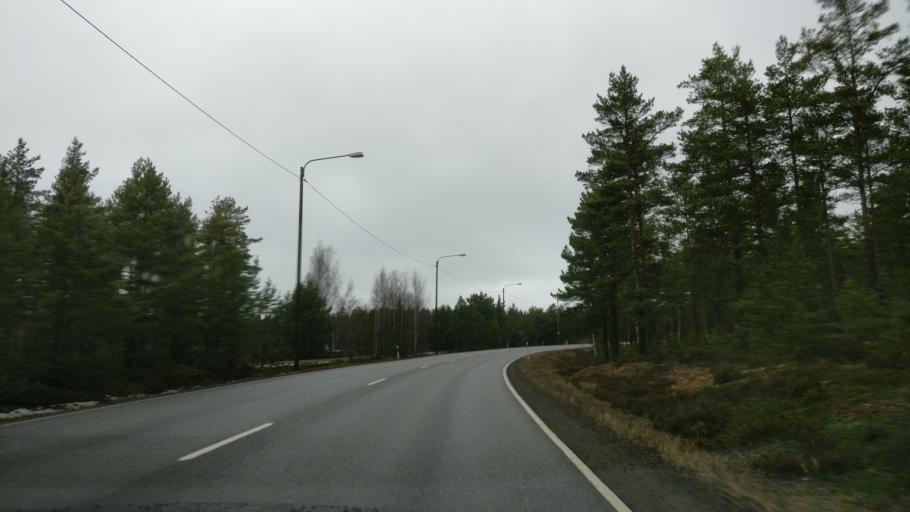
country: FI
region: Uusimaa
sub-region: Raaseporin
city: Hanko
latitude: 59.8486
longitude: 23.0050
